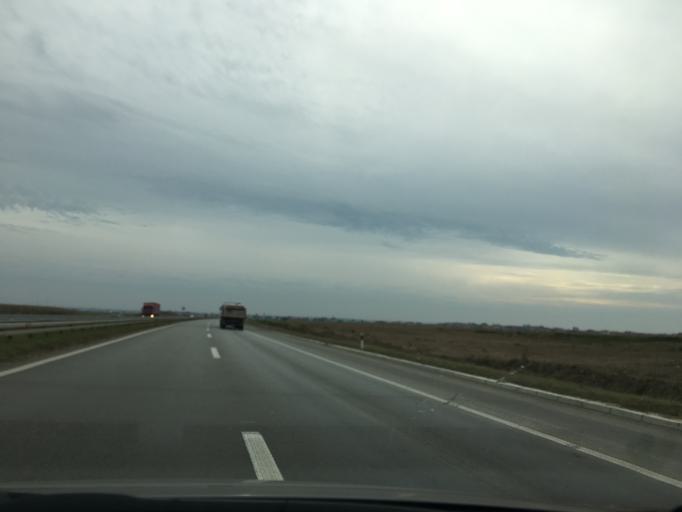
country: RS
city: Novi Banovci
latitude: 44.9152
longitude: 20.3053
